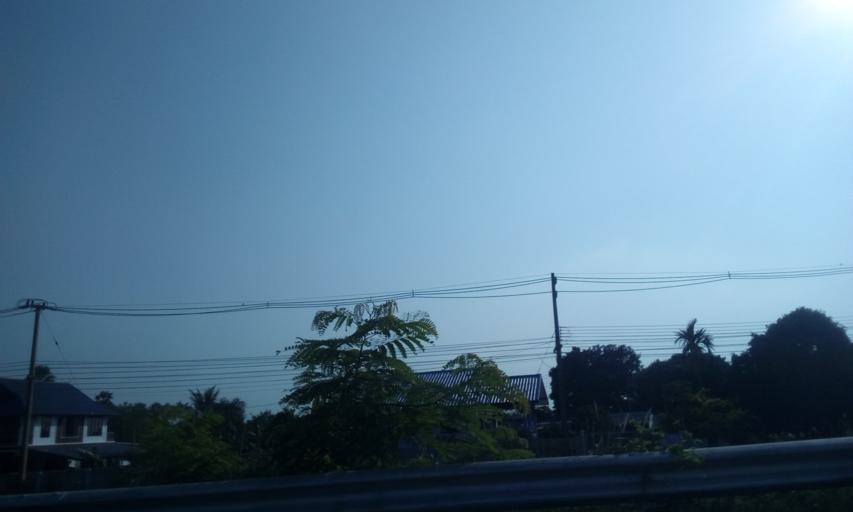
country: TH
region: Sing Buri
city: Sing Buri
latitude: 14.8437
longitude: 100.4257
